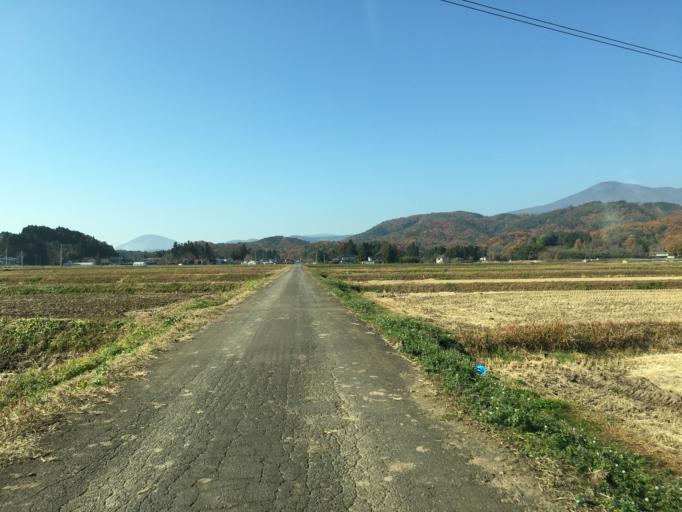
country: JP
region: Fukushima
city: Motomiya
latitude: 37.5584
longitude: 140.3889
